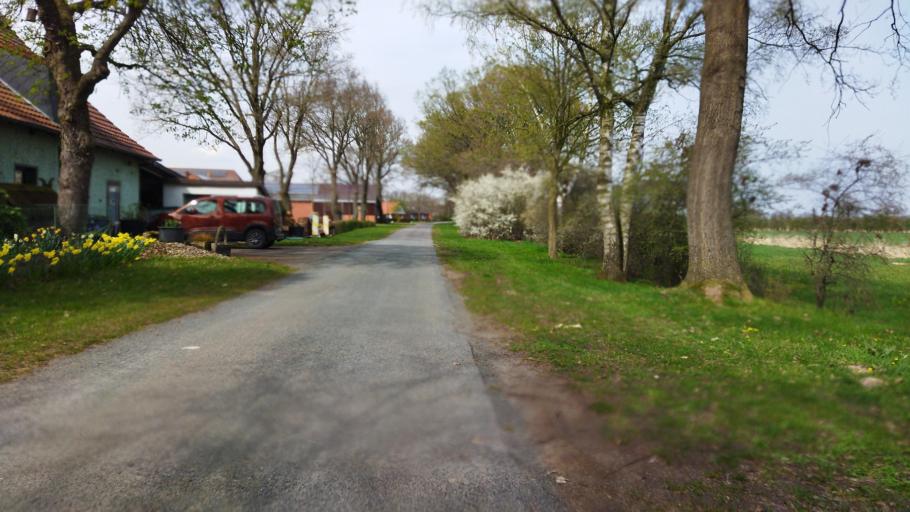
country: DE
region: Lower Saxony
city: Raddestorf
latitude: 52.4362
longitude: 8.9826
